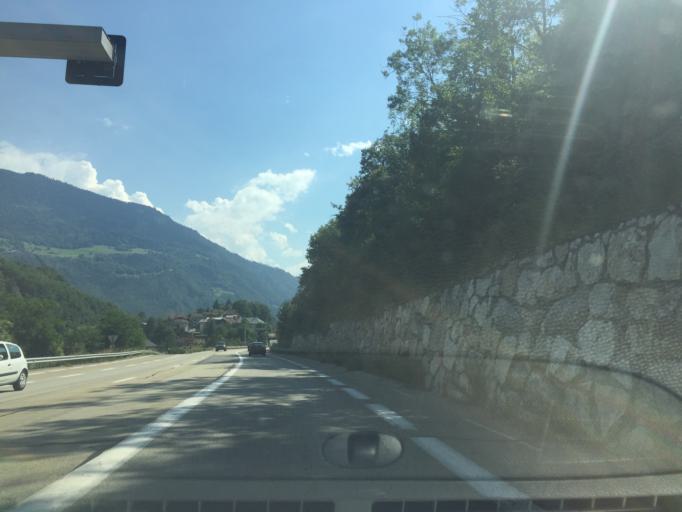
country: FR
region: Rhone-Alpes
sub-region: Departement de la Savoie
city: Moutiers
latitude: 45.5165
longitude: 6.5685
